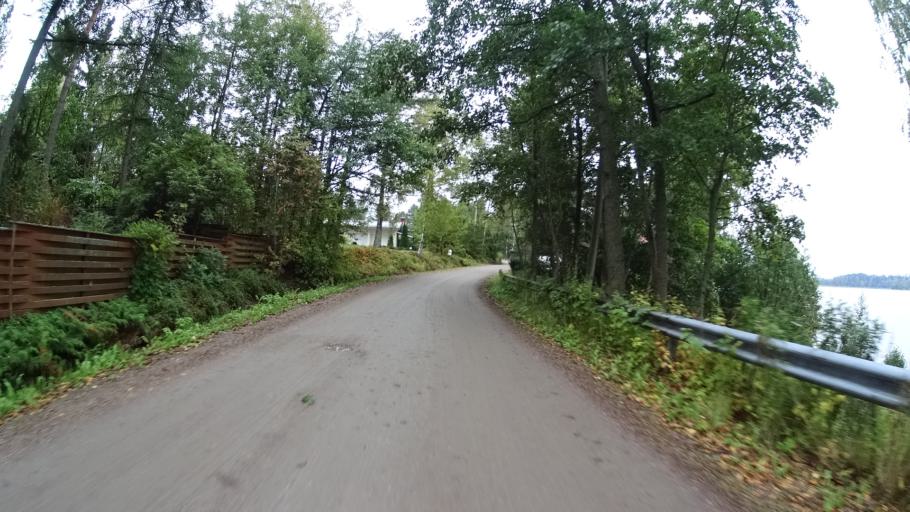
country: FI
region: Uusimaa
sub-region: Helsinki
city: Kilo
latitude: 60.2512
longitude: 24.7552
